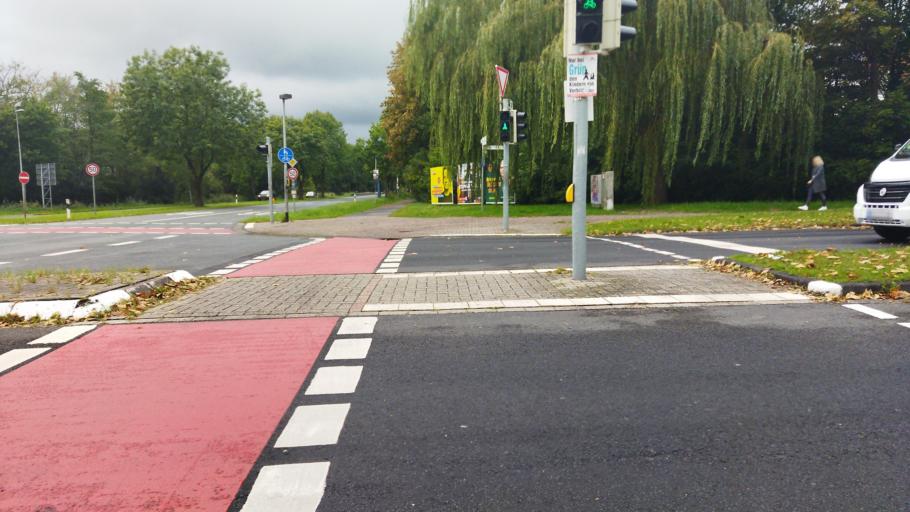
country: DE
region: Lower Saxony
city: Emden
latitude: 53.3660
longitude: 7.1816
